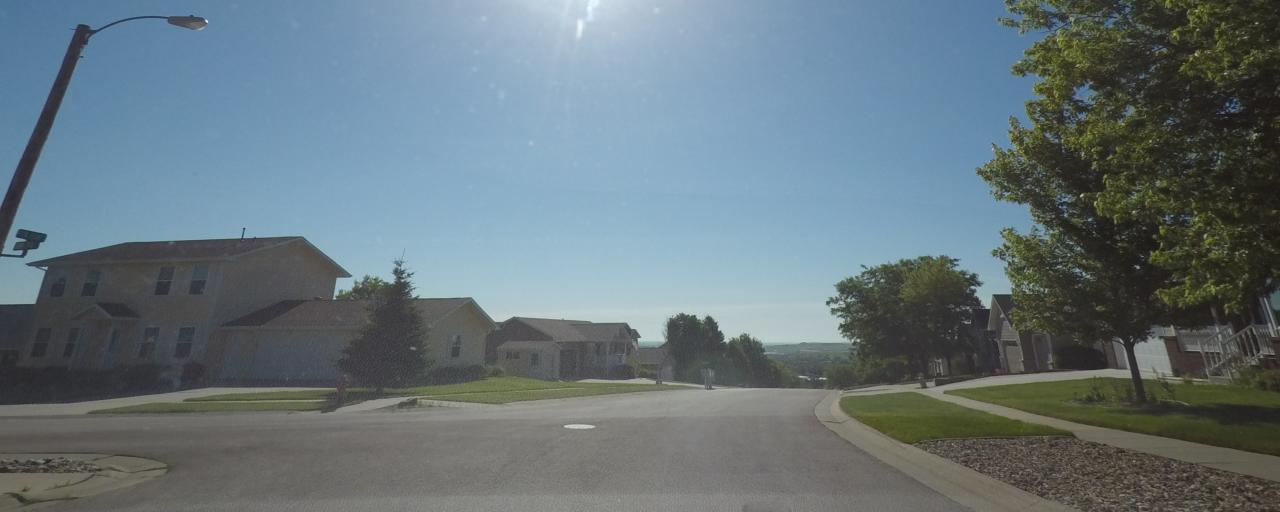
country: US
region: South Dakota
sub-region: Pennington County
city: Rapid City
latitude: 44.0515
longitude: -103.2296
